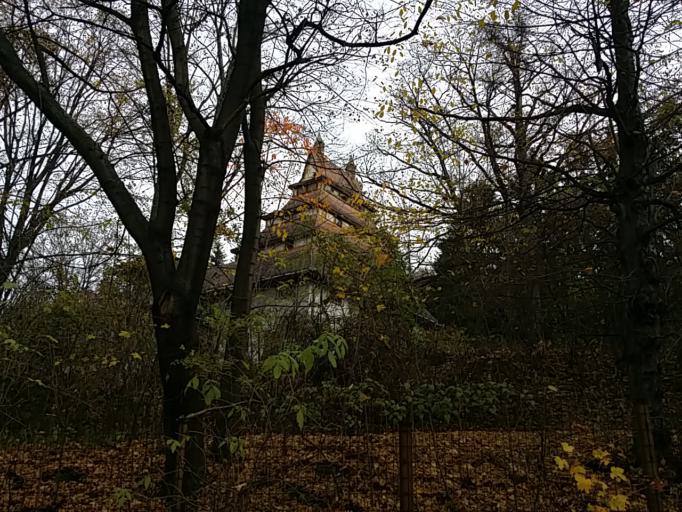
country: HU
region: Heves
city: Paradsasvar
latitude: 47.8706
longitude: 19.9788
